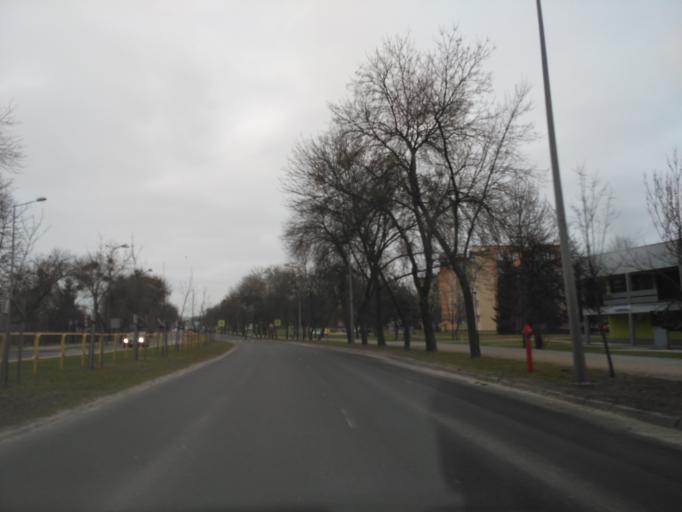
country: PL
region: Lublin Voivodeship
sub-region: Chelm
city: Chelm
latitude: 51.1286
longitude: 23.4731
